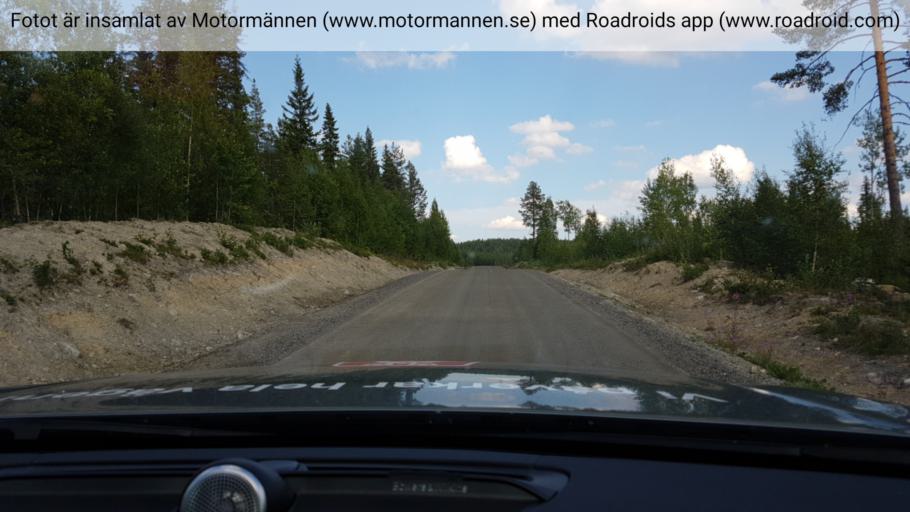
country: SE
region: Vaesterbotten
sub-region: Dorotea Kommun
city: Dorotea
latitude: 63.9294
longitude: 16.1329
